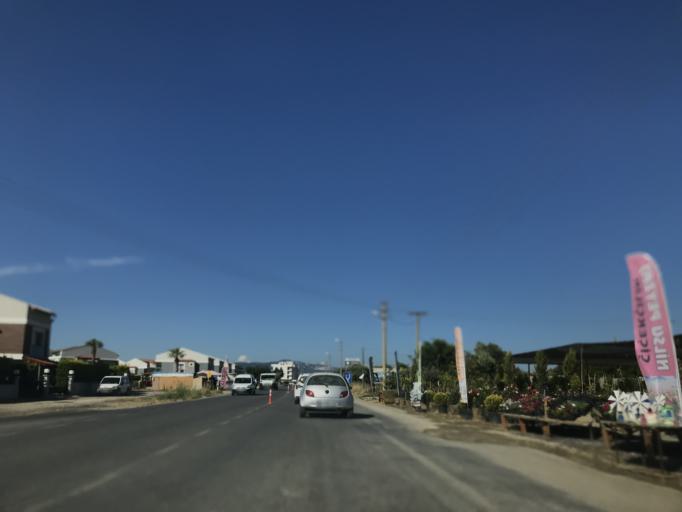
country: TR
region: Aydin
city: Davutlar
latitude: 37.7309
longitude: 27.2712
